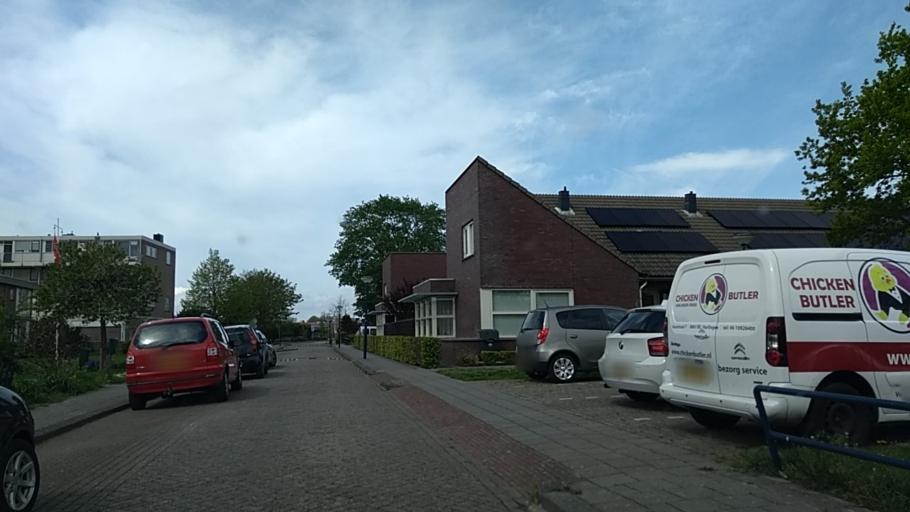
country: NL
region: Friesland
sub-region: Gemeente Harlingen
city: Harlingen
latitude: 53.1683
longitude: 5.4334
